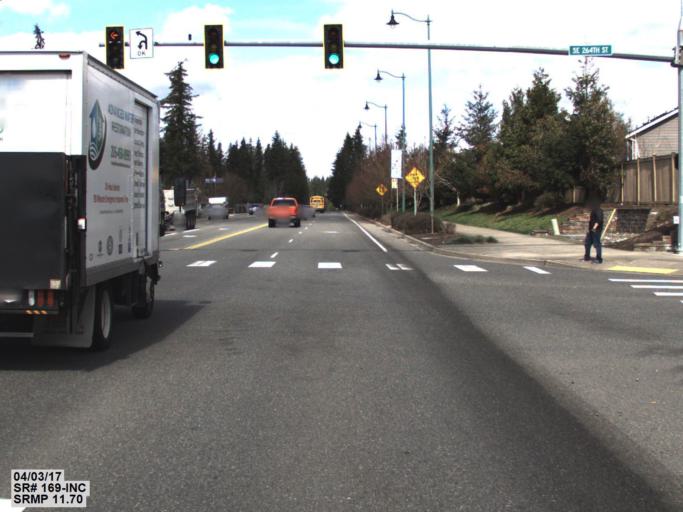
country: US
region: Washington
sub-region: King County
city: Maple Valley
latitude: 47.3652
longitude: -122.0217
